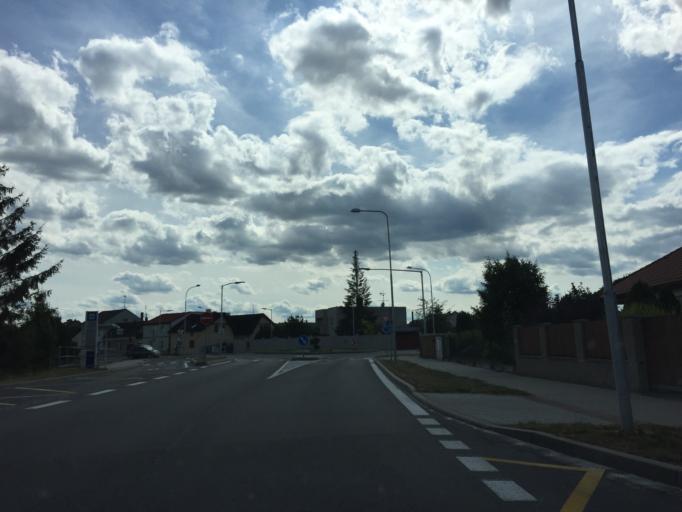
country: CZ
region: Jihocesky
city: Vcelna
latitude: 48.9413
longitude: 14.4784
